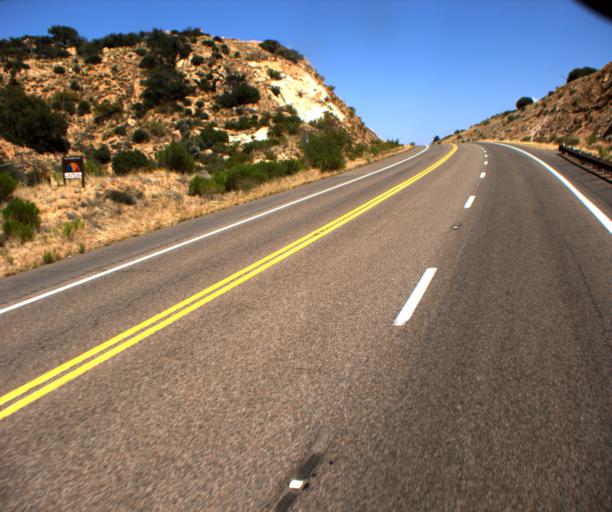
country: US
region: Arizona
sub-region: Gila County
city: Miami
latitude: 33.5375
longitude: -110.9332
